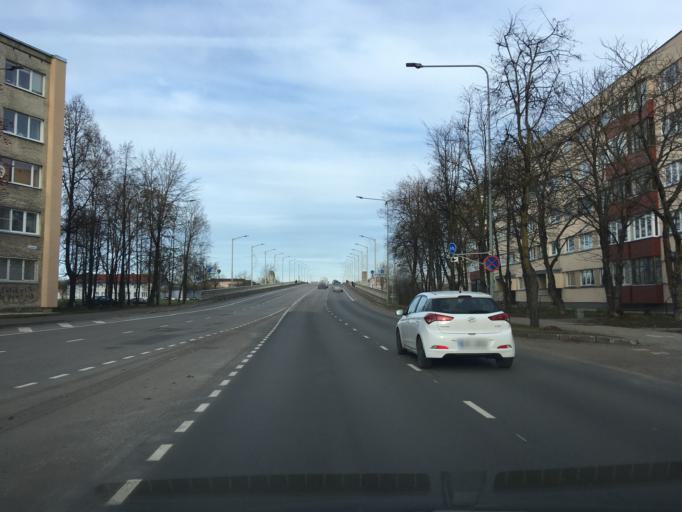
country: EE
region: Ida-Virumaa
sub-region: Narva linn
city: Narva
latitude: 59.3693
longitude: 28.1854
